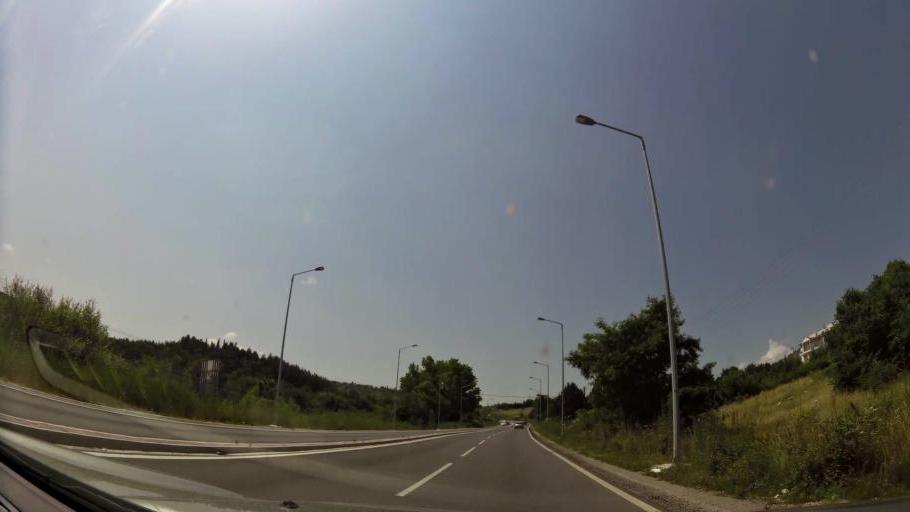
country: GR
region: West Macedonia
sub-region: Nomos Kozanis
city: Koila
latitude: 40.3244
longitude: 21.7881
